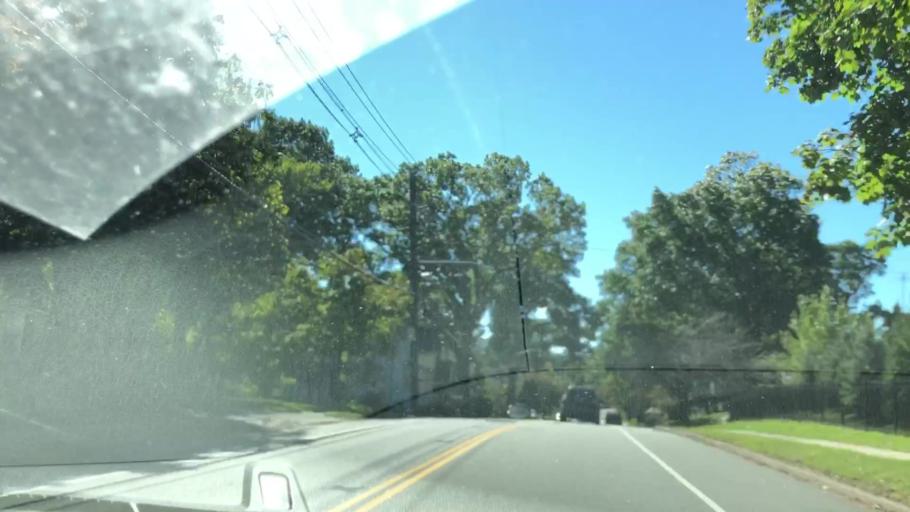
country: US
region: New Jersey
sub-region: Essex County
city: West Orange
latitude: 40.7990
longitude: -74.2263
